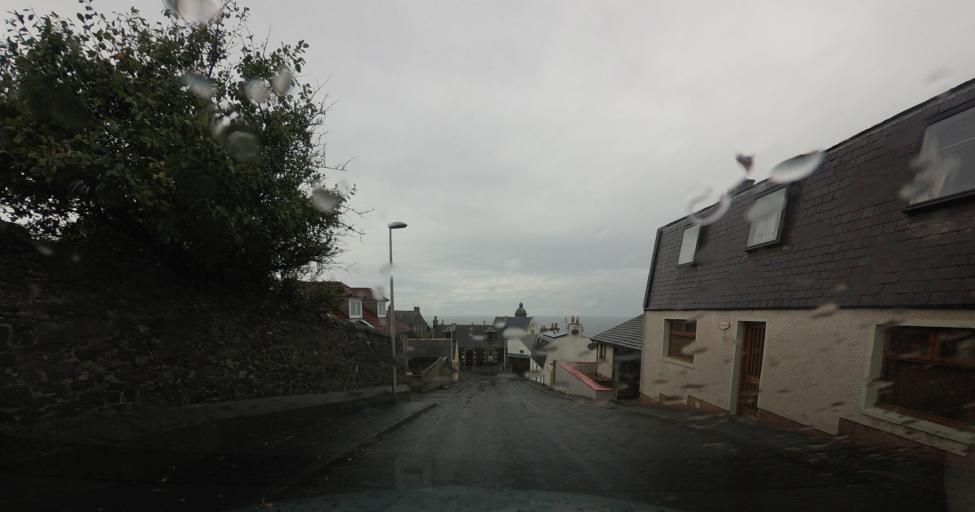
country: GB
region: Scotland
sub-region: Aberdeenshire
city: Macduff
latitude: 57.6668
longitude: -2.4988
